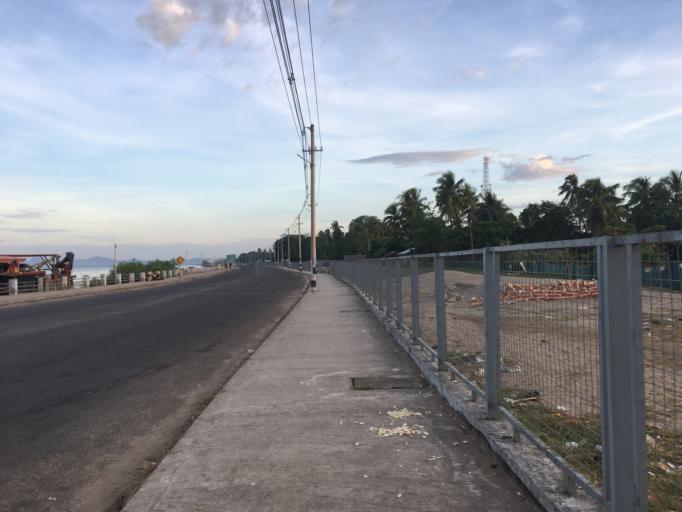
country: MM
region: Mon
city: Mawlamyine
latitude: 16.4569
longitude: 97.6236
